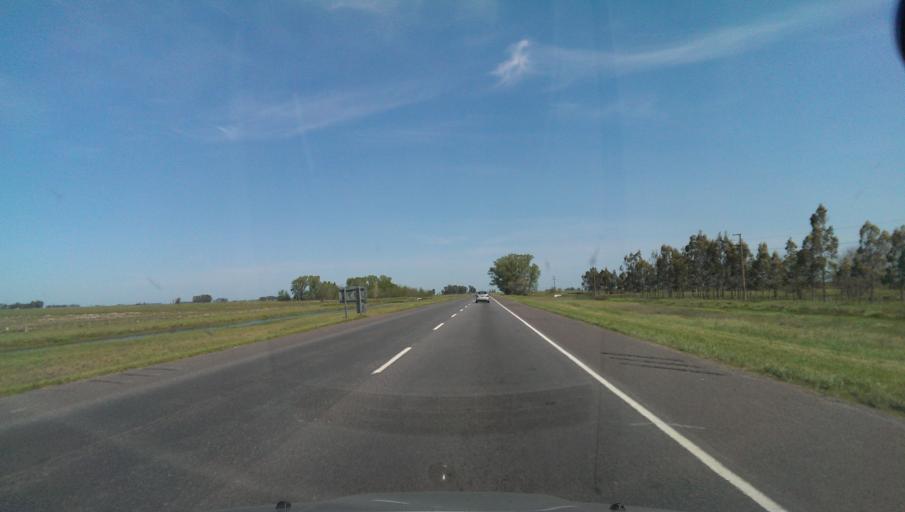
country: AR
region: Buenos Aires
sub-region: Partido de Azul
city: Azul
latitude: -36.4948
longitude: -59.5931
